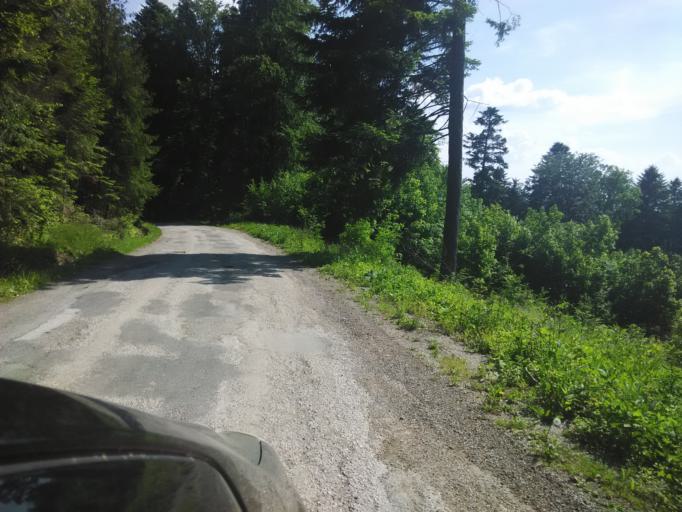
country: SK
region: Kosicky
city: Dobsina
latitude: 48.6579
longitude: 20.2954
